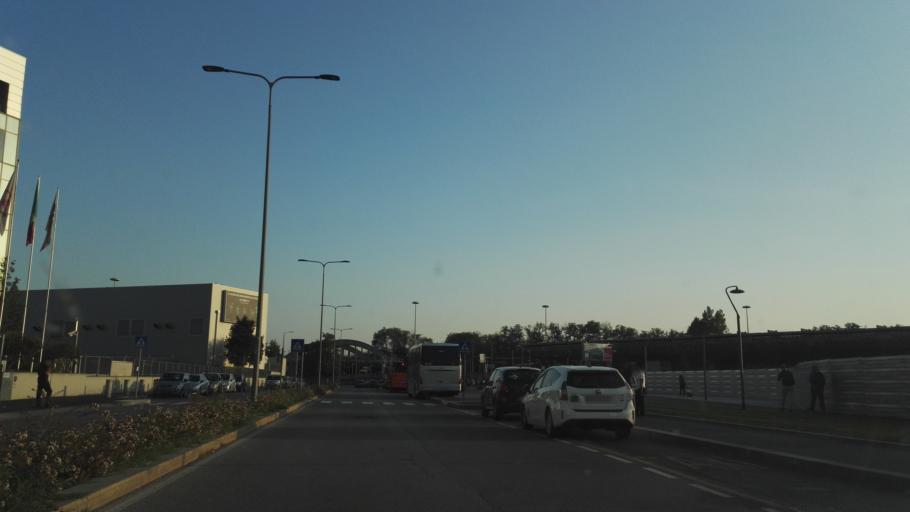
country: IT
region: Lombardy
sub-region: Citta metropolitana di Milano
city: Chiaravalle
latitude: 45.4340
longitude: 9.2407
